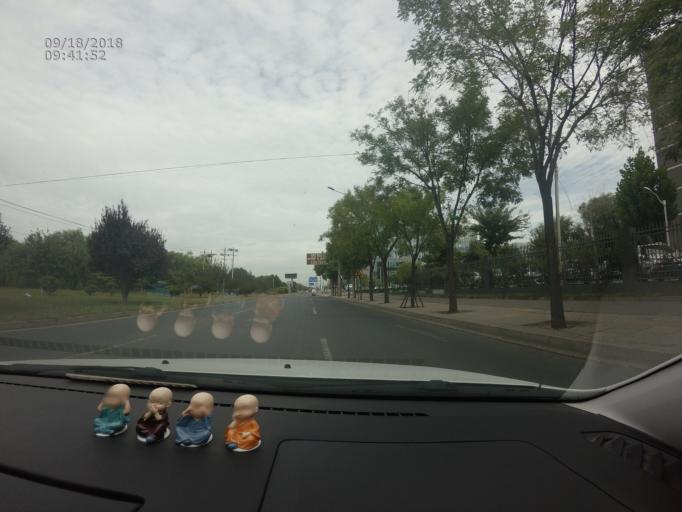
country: CN
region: Beijing
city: Xibeiwang
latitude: 40.0694
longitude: 116.2399
